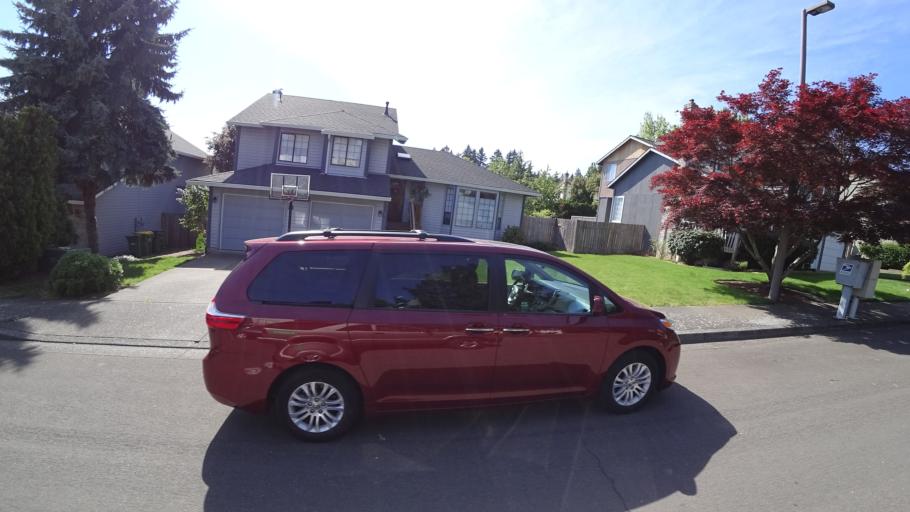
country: US
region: Oregon
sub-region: Washington County
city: Aloha
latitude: 45.4678
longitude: -122.8448
